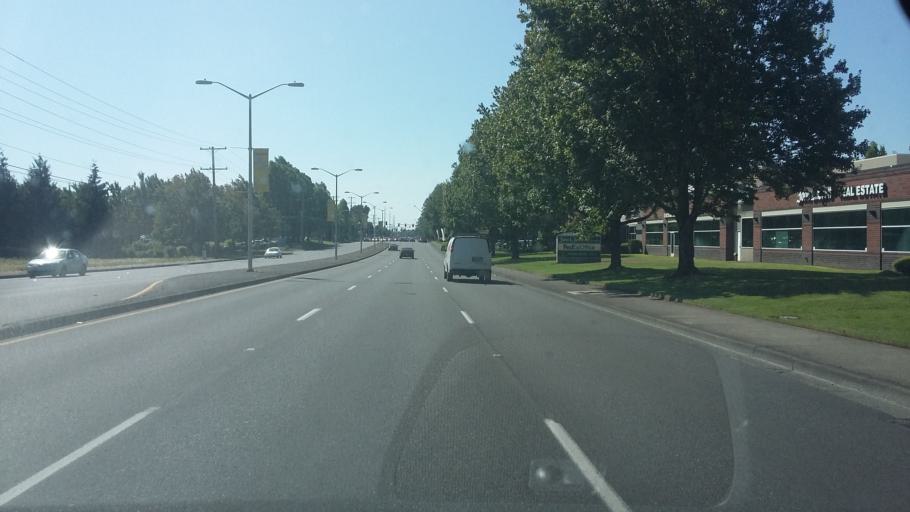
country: US
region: Washington
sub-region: Clark County
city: Mill Plain
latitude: 45.6194
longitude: -122.5389
